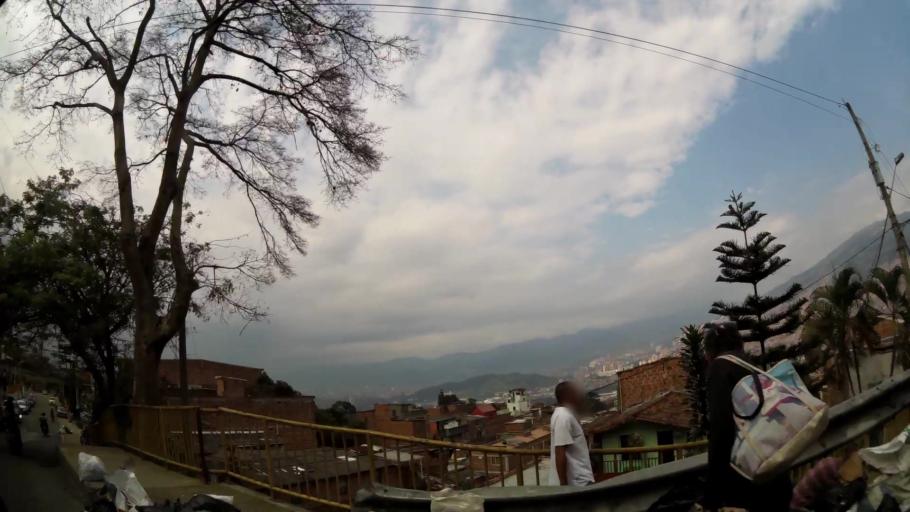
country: CO
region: Antioquia
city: Medellin
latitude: 6.2888
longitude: -75.5732
